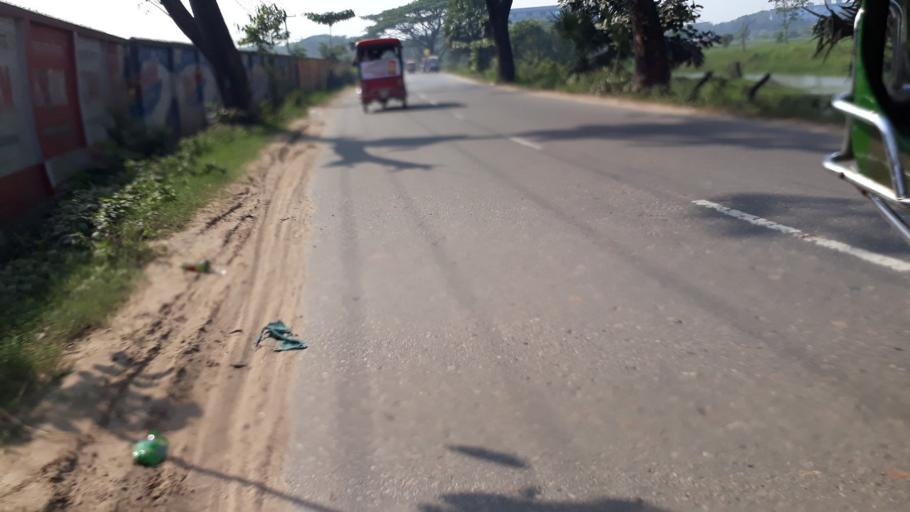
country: BD
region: Dhaka
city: Tungi
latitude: 23.9022
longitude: 90.2790
